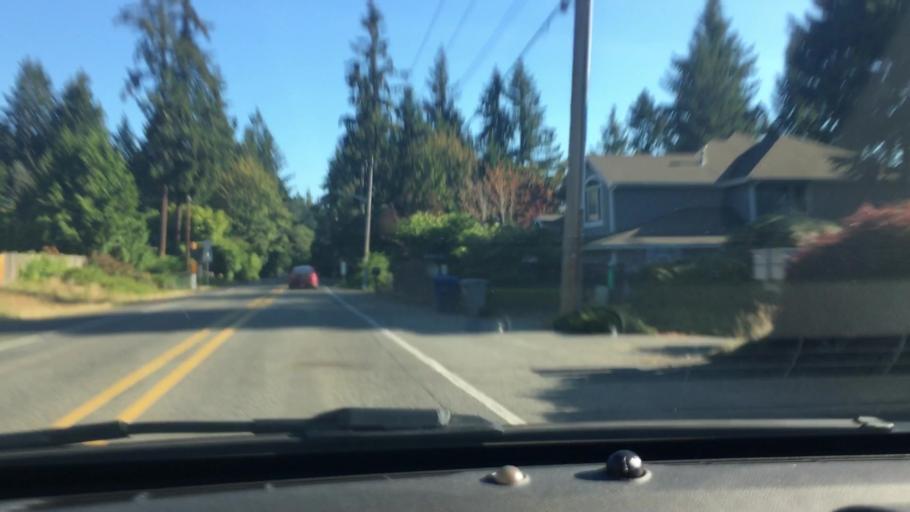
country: US
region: Washington
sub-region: King County
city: West Lake Sammamish
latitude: 47.5871
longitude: -122.1115
